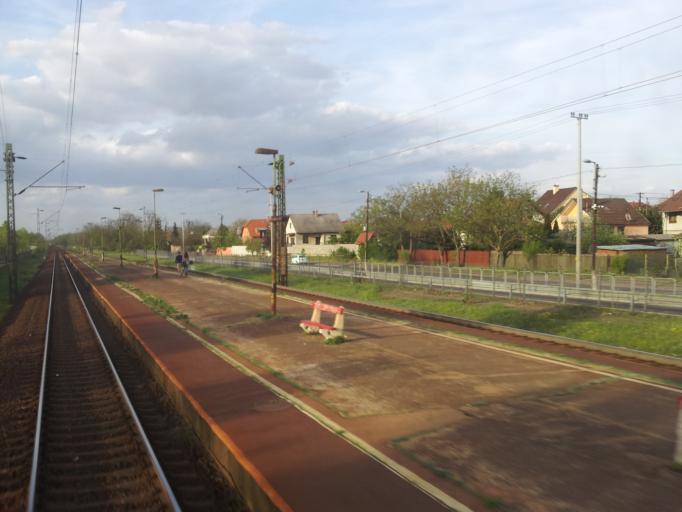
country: HU
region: Pest
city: Dunakeszi
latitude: 47.6078
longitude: 19.1290
